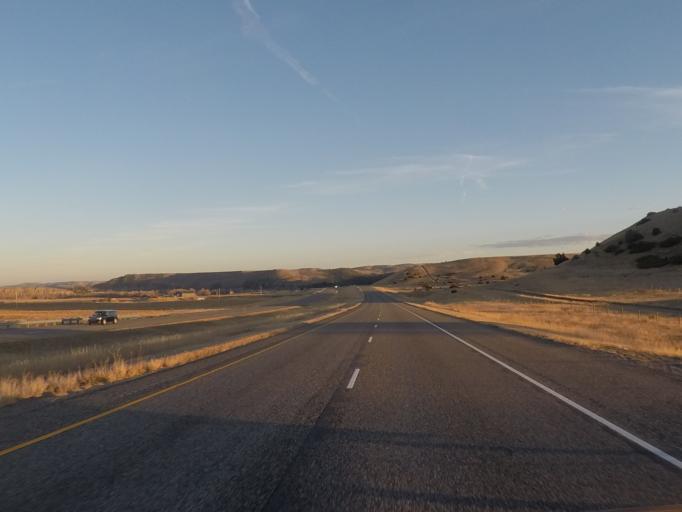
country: US
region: Montana
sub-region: Sweet Grass County
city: Big Timber
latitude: 45.7487
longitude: -109.7753
